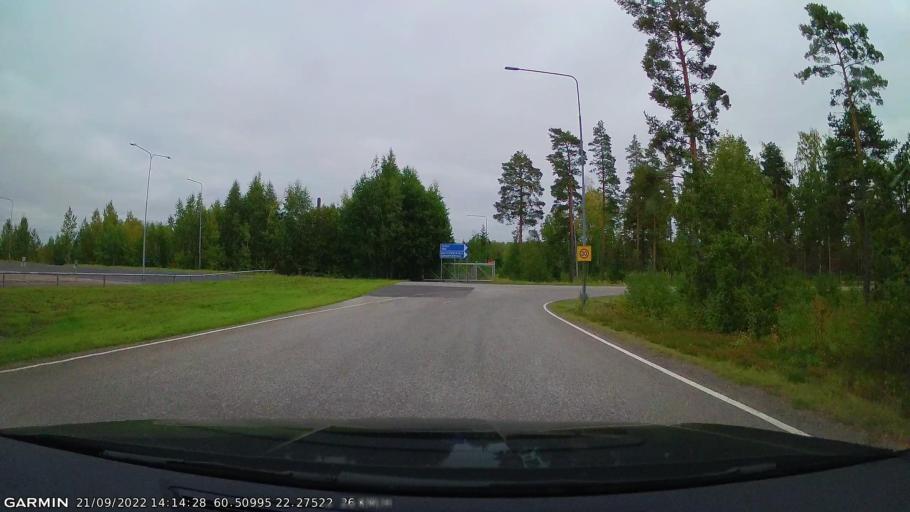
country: FI
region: Varsinais-Suomi
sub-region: Turku
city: Turku
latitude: 60.5102
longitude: 22.2747
